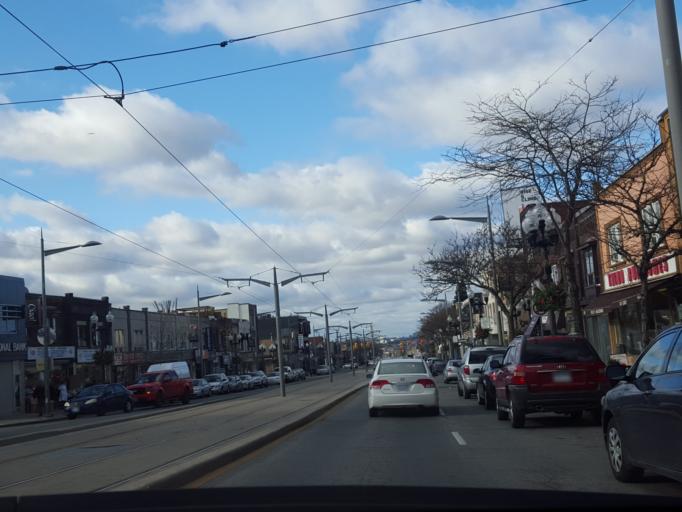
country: CA
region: Ontario
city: Toronto
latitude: 43.6770
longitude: -79.4478
